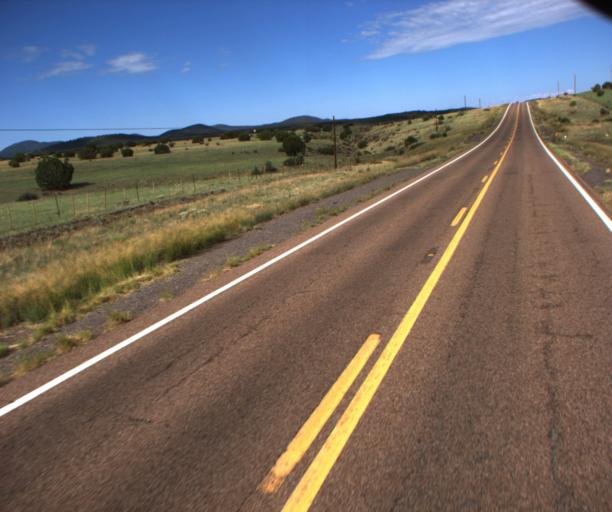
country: US
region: Arizona
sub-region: Navajo County
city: Pinetop-Lakeside
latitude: 34.2705
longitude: -109.6421
